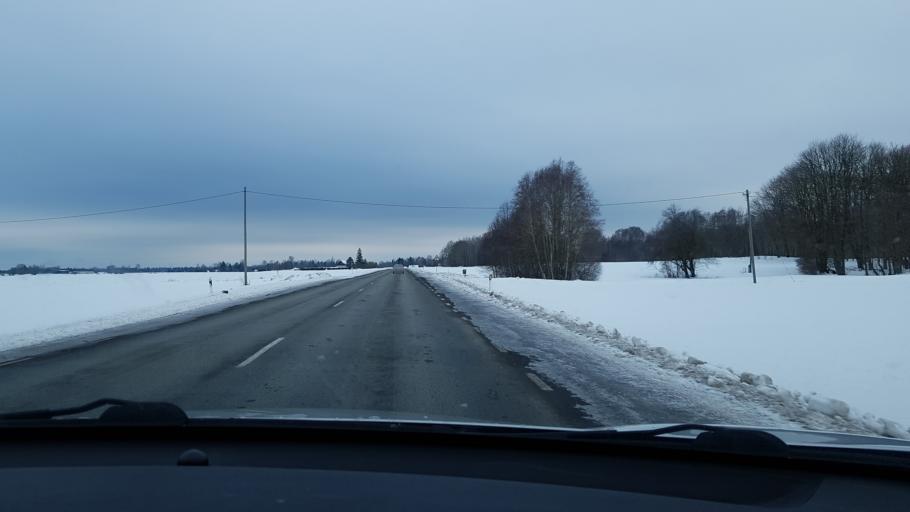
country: EE
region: Jaervamaa
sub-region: Paide linn
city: Paide
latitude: 58.8847
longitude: 25.7081
